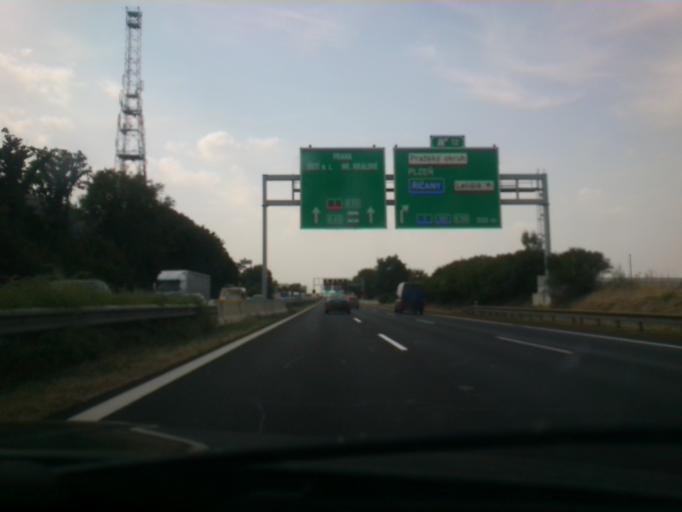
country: CZ
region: Central Bohemia
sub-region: Okres Praha-Vychod
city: Ricany
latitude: 49.9639
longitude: 14.6269
